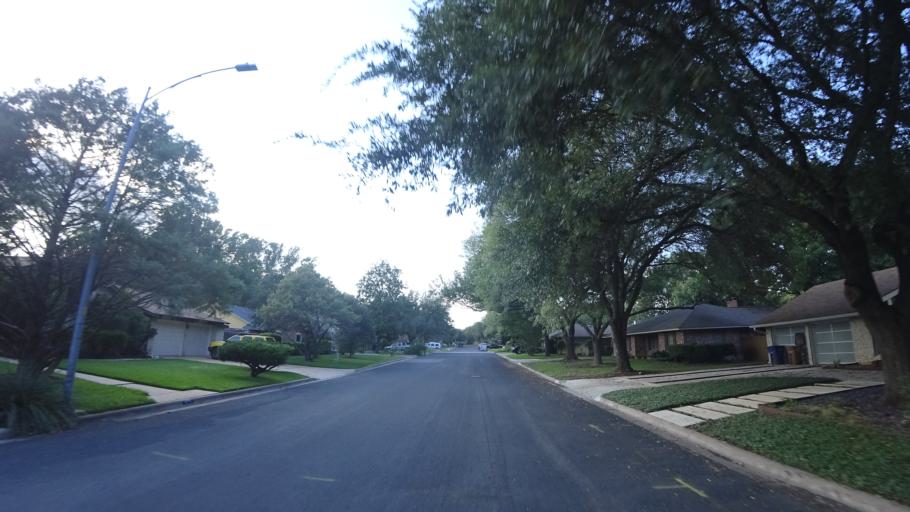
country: US
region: Texas
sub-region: Travis County
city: Wells Branch
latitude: 30.3633
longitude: -97.7022
